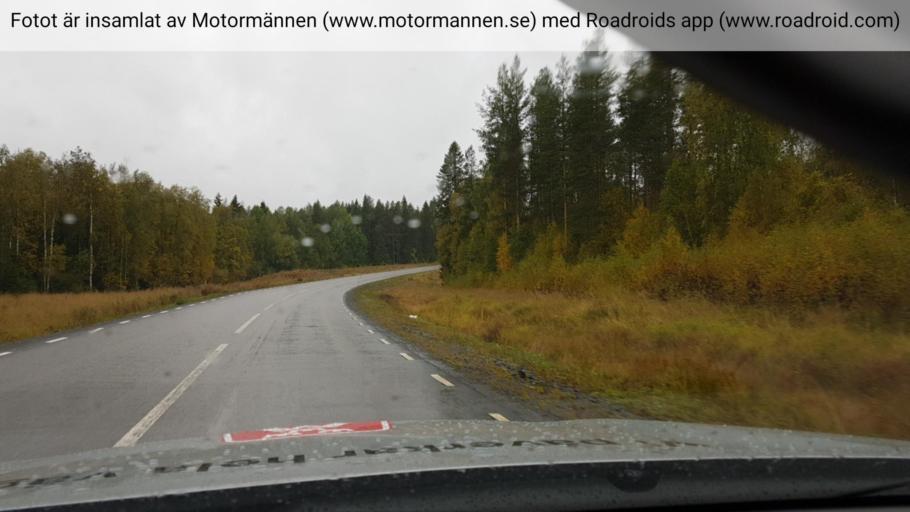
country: SE
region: Norrbotten
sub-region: Lulea Kommun
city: Sodra Sunderbyn
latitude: 65.8207
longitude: 21.9163
